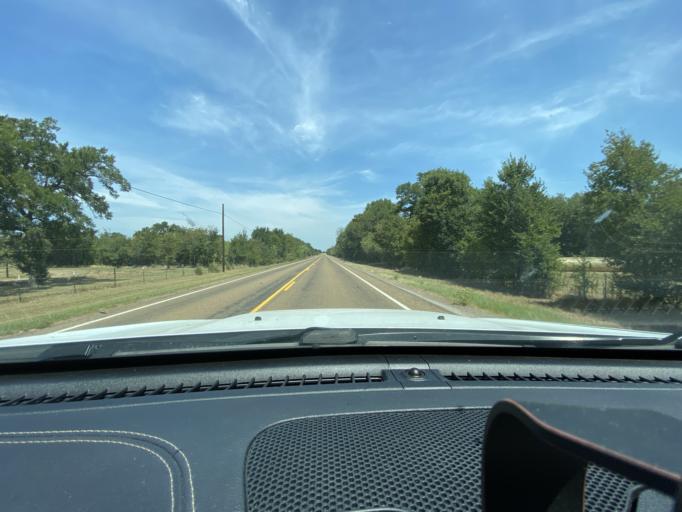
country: US
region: Texas
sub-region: Bastrop County
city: Smithville
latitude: 30.1050
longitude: -97.0781
